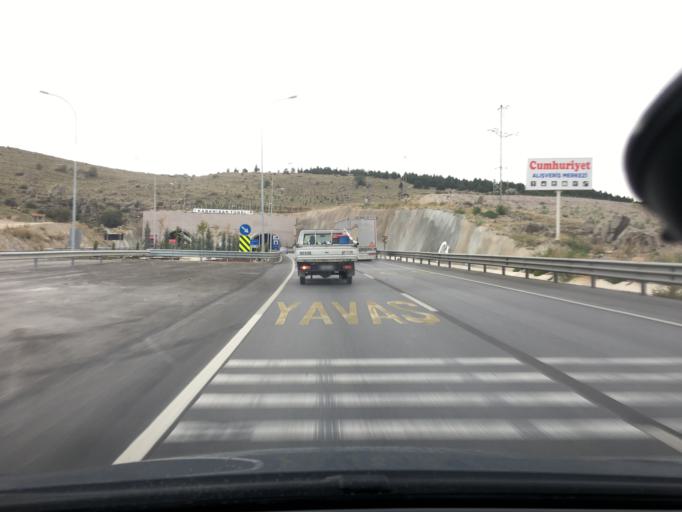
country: TR
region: Afyonkarahisar
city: Afyonkarahisar
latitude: 38.7951
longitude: 30.4389
